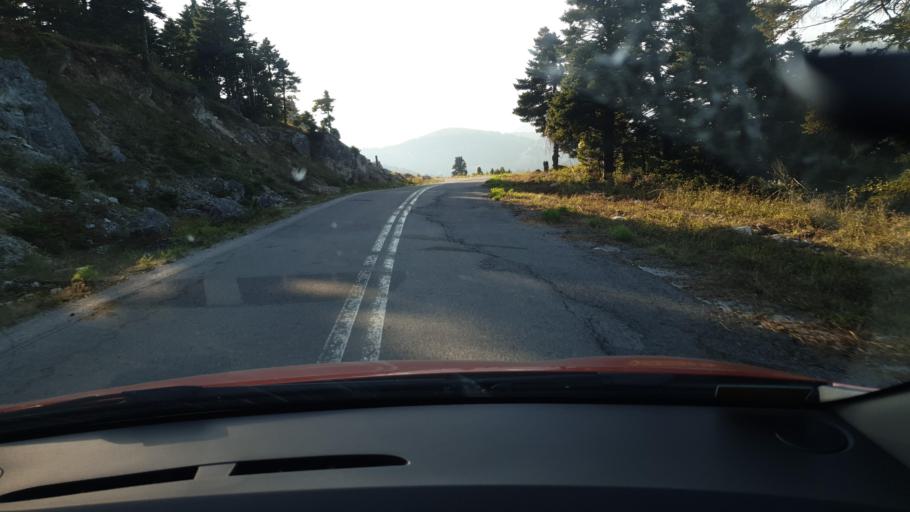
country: GR
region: Central Greece
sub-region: Nomos Evvoias
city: Yimnon
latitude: 38.5935
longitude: 23.8914
